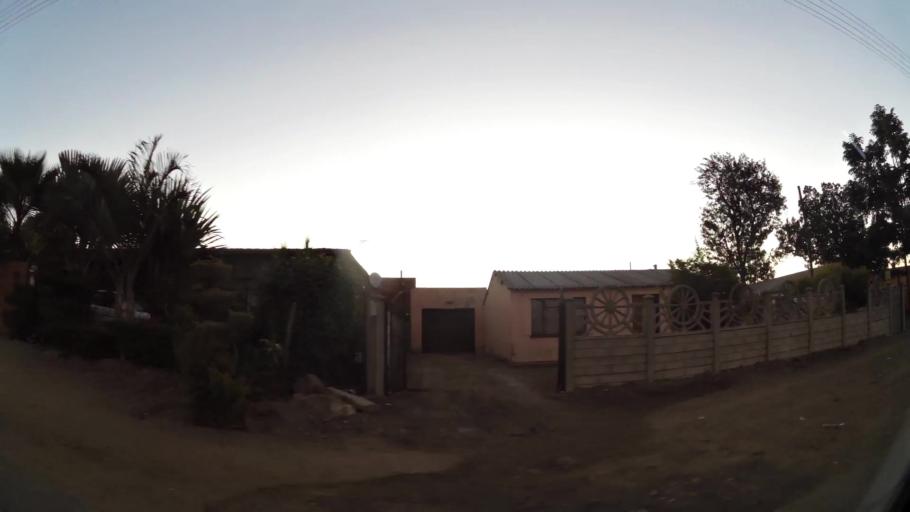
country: ZA
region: Limpopo
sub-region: Capricorn District Municipality
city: Polokwane
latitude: -23.8511
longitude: 29.3978
